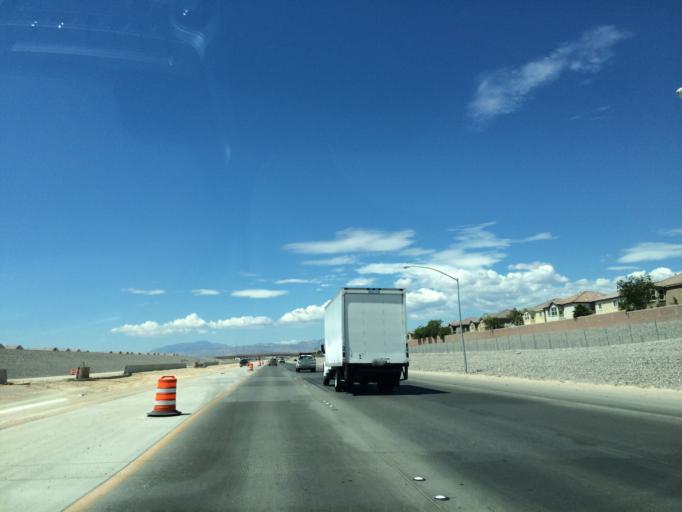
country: US
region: Nevada
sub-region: Clark County
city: North Las Vegas
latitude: 36.2867
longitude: -115.1844
